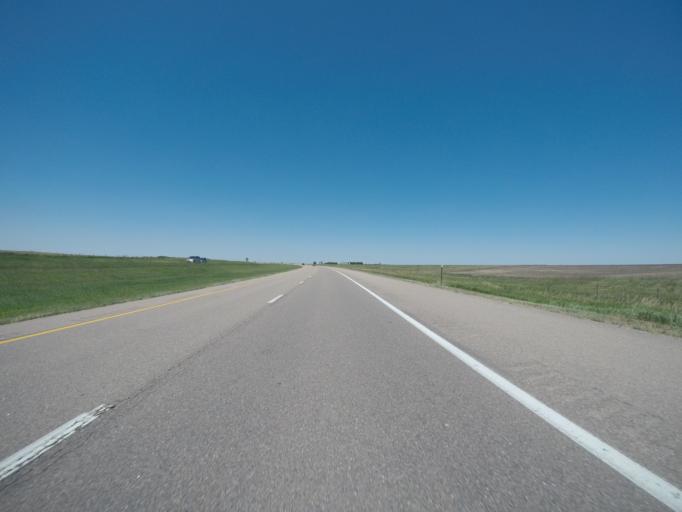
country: US
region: Kansas
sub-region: Gove County
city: Gove
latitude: 39.0962
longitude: -100.3230
